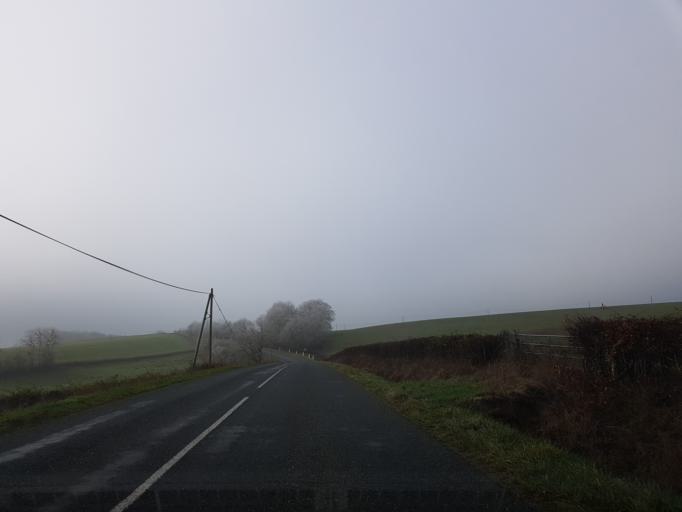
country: FR
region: Bourgogne
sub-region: Departement de Saone-et-Loire
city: Toulon-sur-Arroux
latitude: 46.7042
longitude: 4.2042
